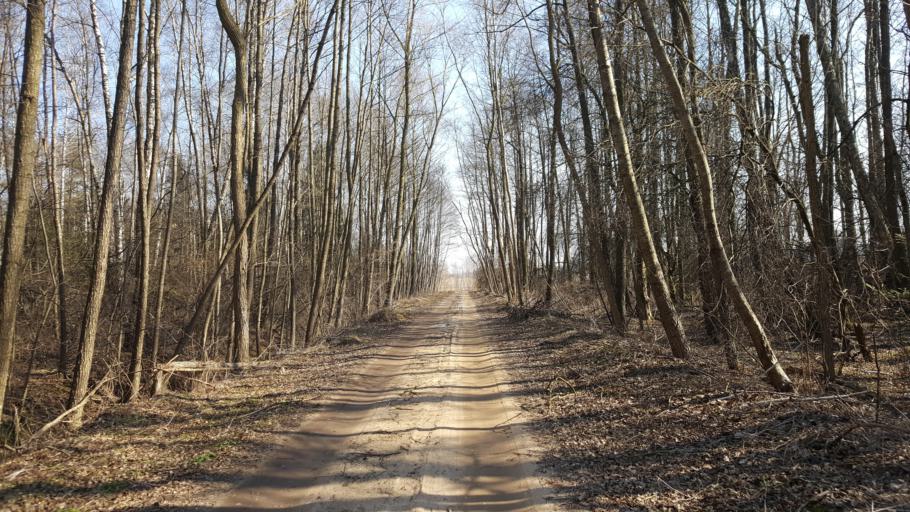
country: BY
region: Brest
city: Kamyanyets
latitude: 52.3660
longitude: 23.7548
